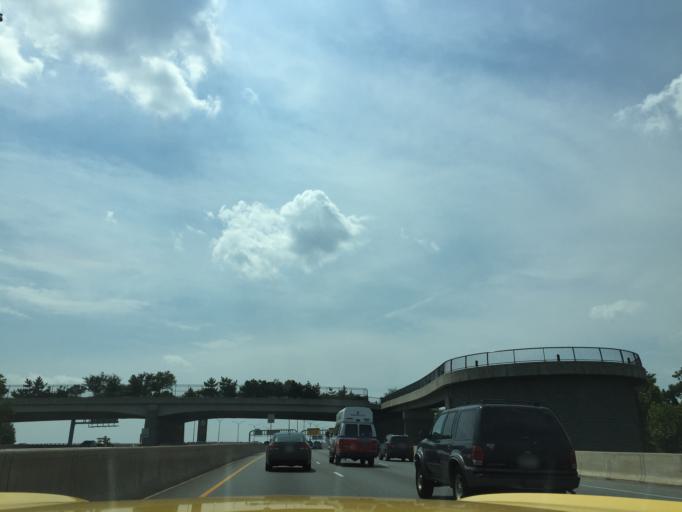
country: US
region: Virginia
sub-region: City of Alexandria
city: Alexandria
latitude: 38.7936
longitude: -77.0230
